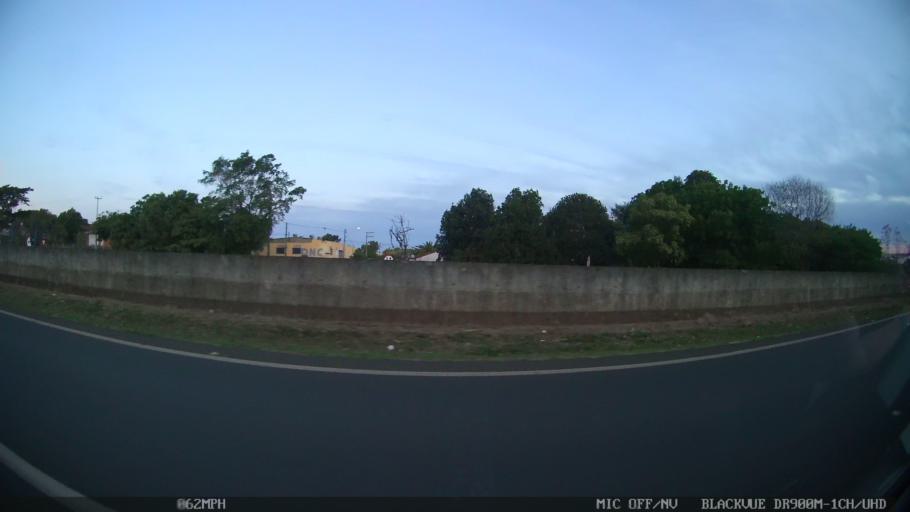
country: BR
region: Sao Paulo
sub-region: Catanduva
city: Catanduva
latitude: -21.1127
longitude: -48.9717
